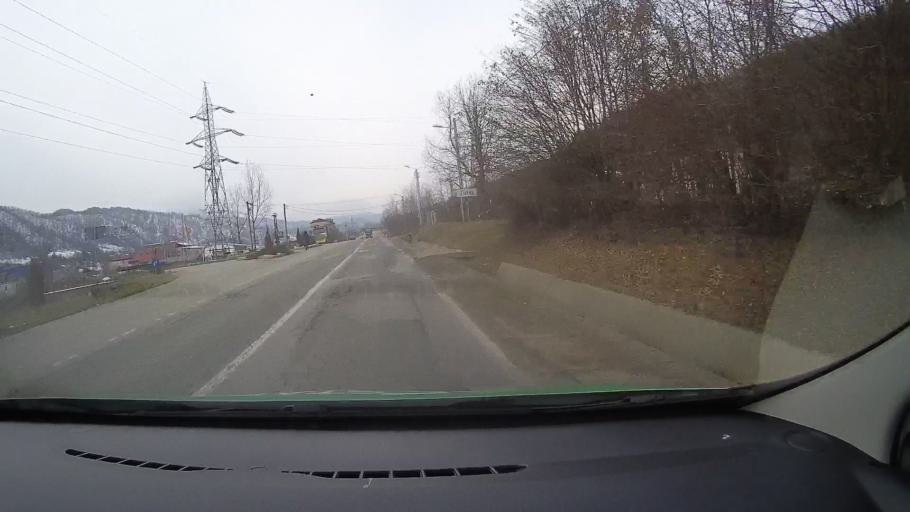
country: RO
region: Alba
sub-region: Oras Zlatna
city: Zlatna
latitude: 46.1054
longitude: 23.2426
